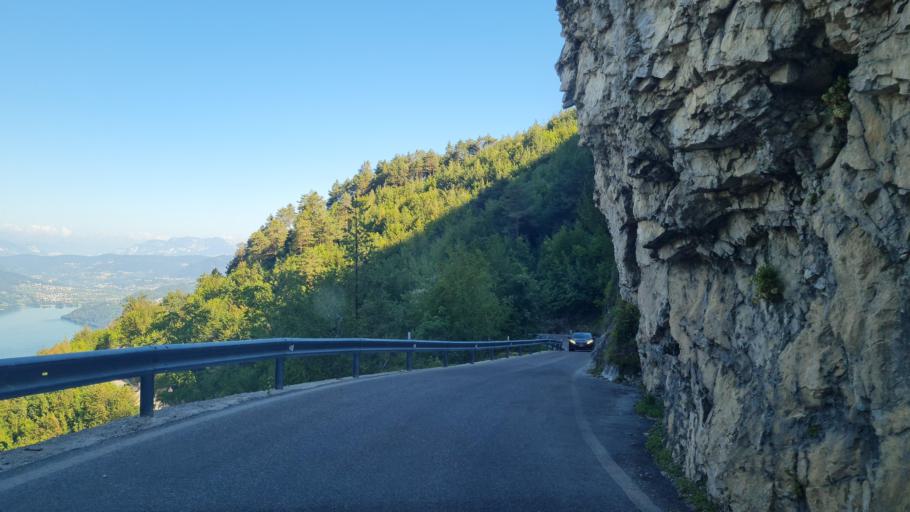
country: IT
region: Trentino-Alto Adige
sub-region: Provincia di Trento
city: Caldonazzo
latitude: 45.9745
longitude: 11.2885
